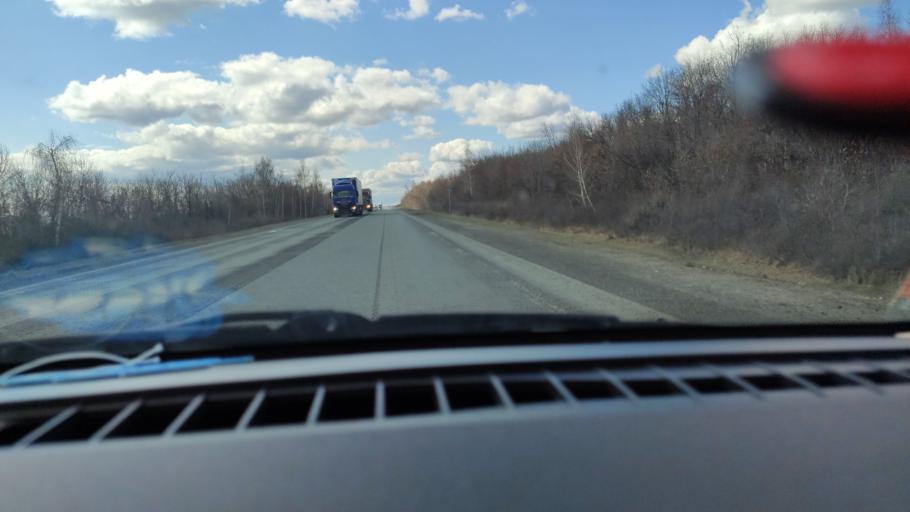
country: RU
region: Saratov
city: Dukhovnitskoye
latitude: 52.6375
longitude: 48.1891
